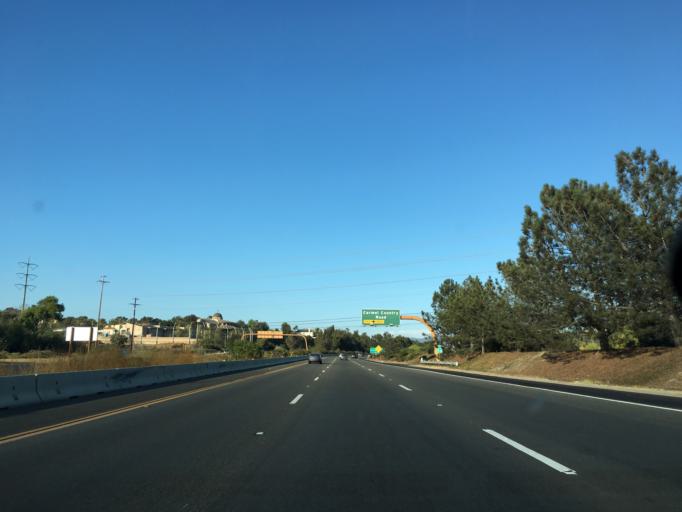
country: US
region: California
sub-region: San Diego County
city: Del Mar
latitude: 32.9390
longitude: -117.2233
